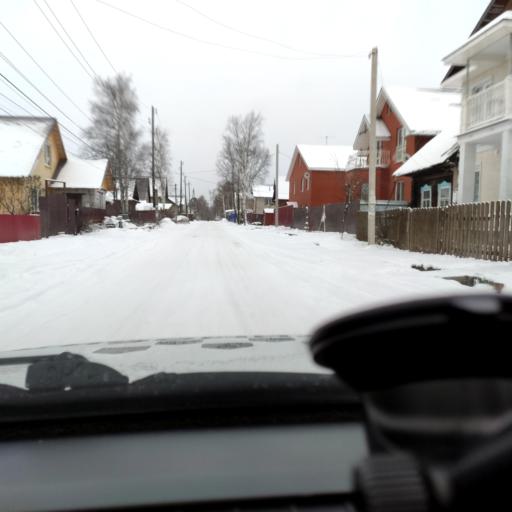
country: RU
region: Perm
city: Perm
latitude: 58.0592
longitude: 56.3637
